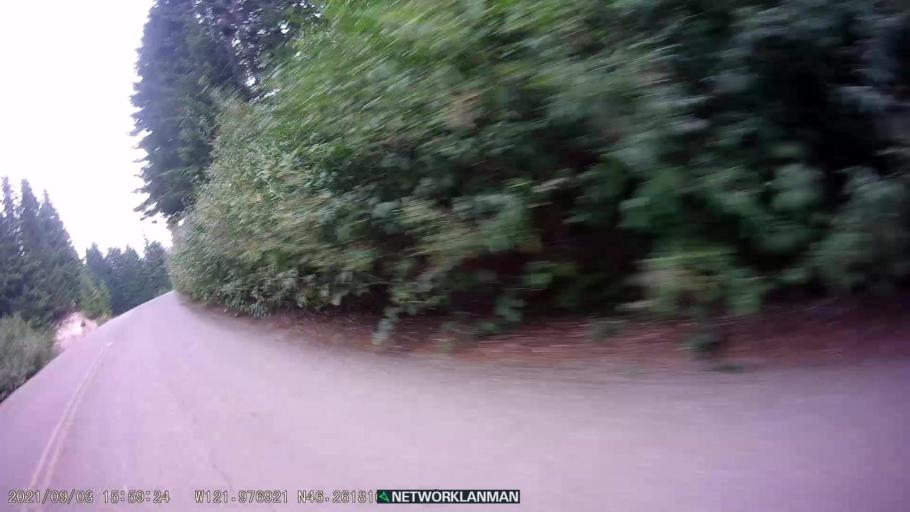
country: US
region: Washington
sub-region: Lewis County
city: Morton
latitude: 46.2620
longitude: -121.9773
